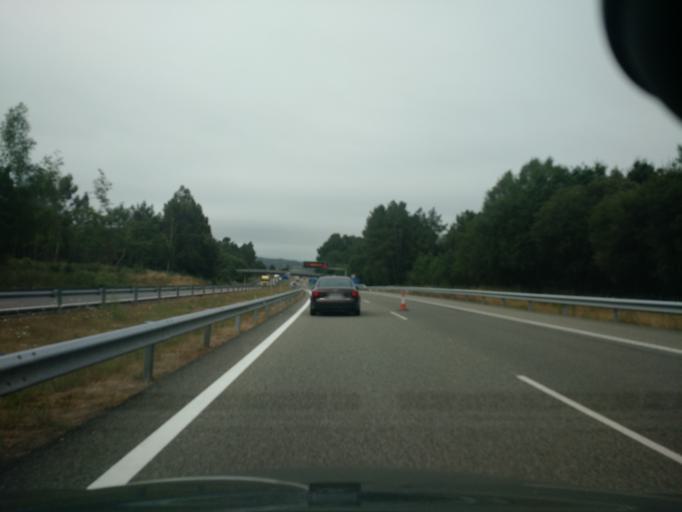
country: ES
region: Galicia
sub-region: Provincia da Coruna
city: Oroso
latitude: 42.9881
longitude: -8.4311
